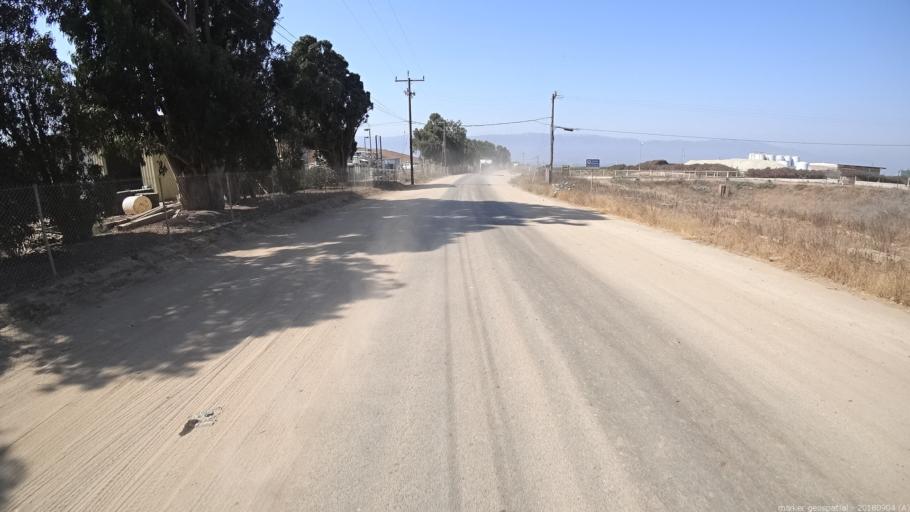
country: US
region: California
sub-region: Monterey County
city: Gonzales
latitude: 36.5337
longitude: -121.4057
